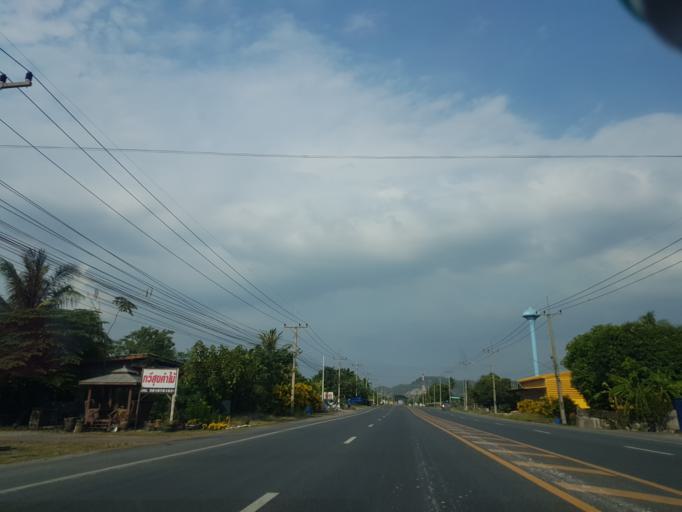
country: TH
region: Sara Buri
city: Ban Mo
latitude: 14.6616
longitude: 100.7673
